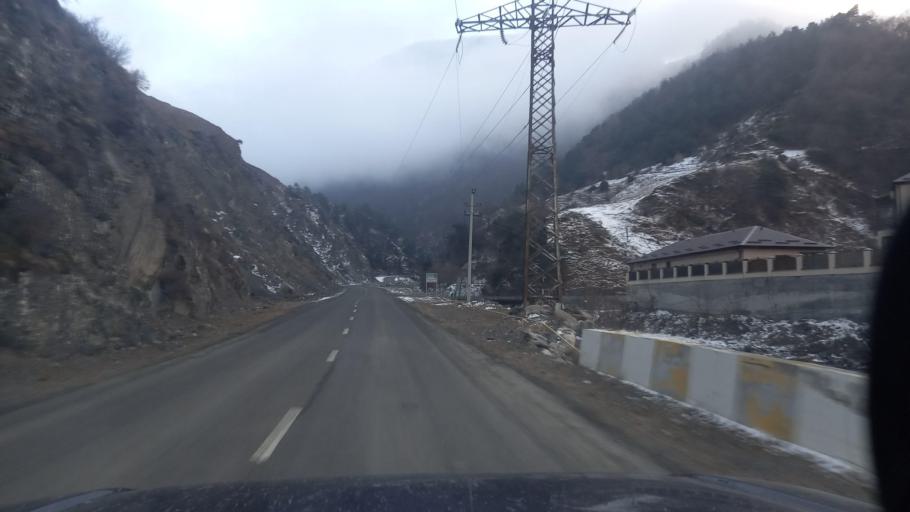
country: RU
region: Ingushetiya
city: Dzhayrakh
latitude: 42.7983
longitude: 44.7609
